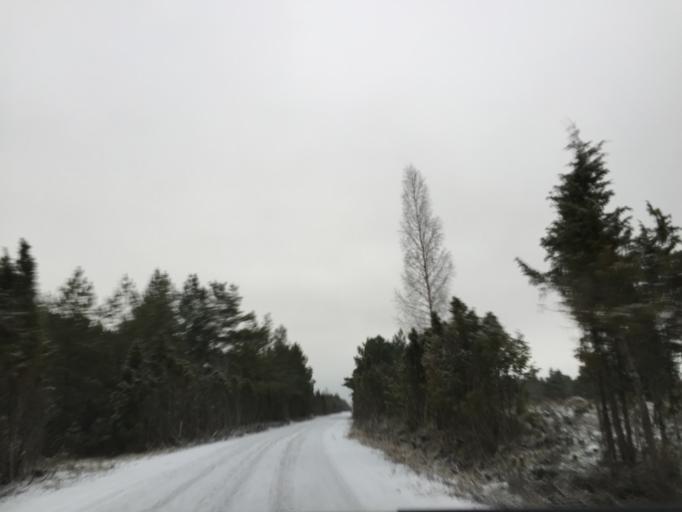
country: EE
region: Saare
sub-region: Orissaare vald
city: Orissaare
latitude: 58.5639
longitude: 23.3869
